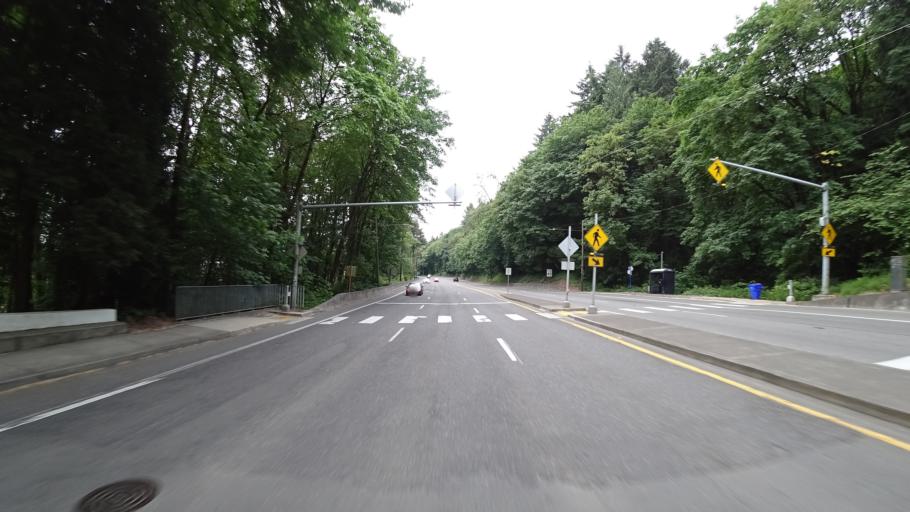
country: US
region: Oregon
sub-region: Multnomah County
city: Portland
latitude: 45.4873
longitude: -122.6826
